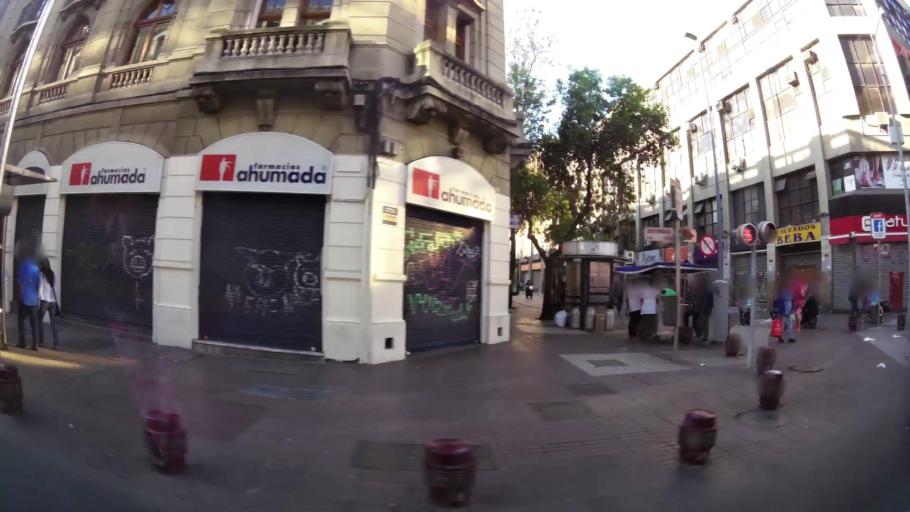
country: CL
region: Santiago Metropolitan
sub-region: Provincia de Santiago
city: Santiago
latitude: -33.4362
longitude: -70.6515
